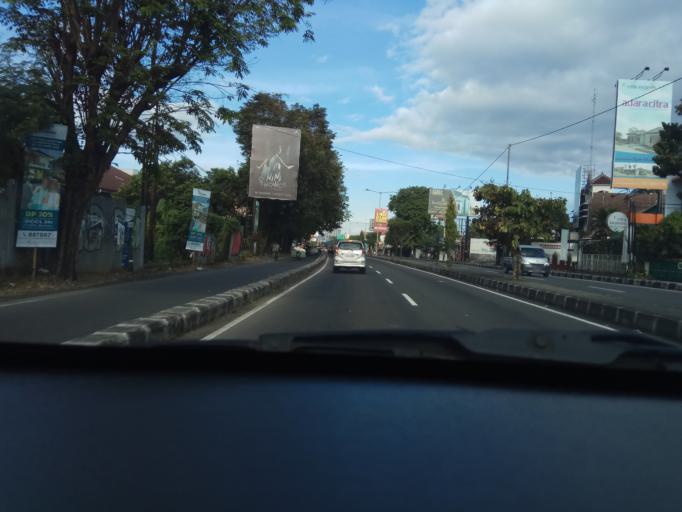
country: ID
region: Daerah Istimewa Yogyakarta
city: Depok
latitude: -7.7582
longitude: 110.3985
